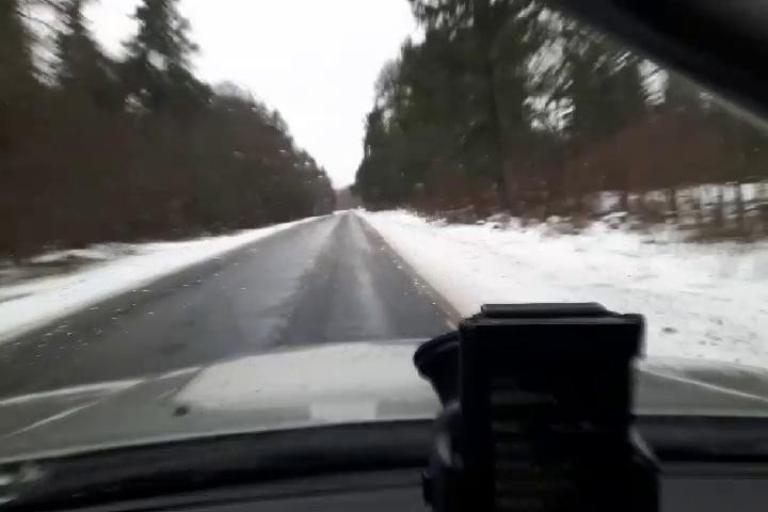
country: EE
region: Harju
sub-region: Harku vald
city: Tabasalu
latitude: 59.4294
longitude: 24.4582
